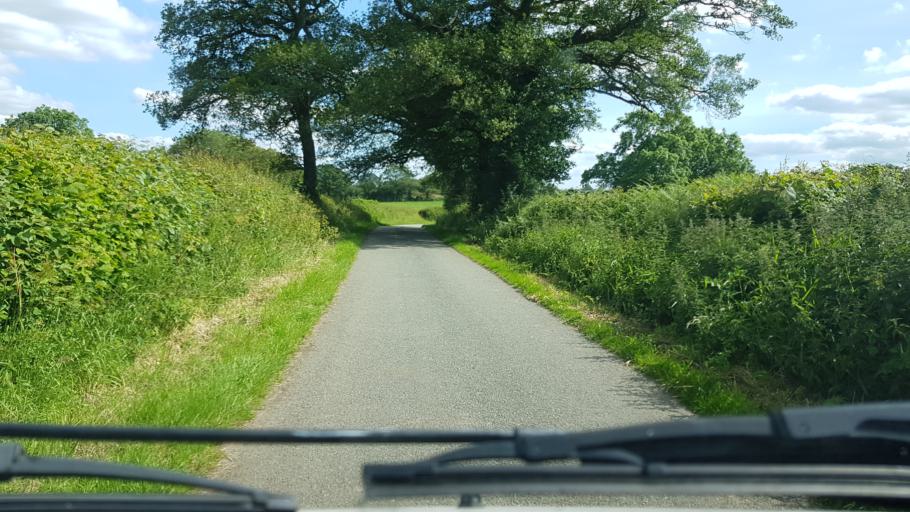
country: GB
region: England
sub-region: Shropshire
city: Romsley
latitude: 52.4557
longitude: -2.2916
